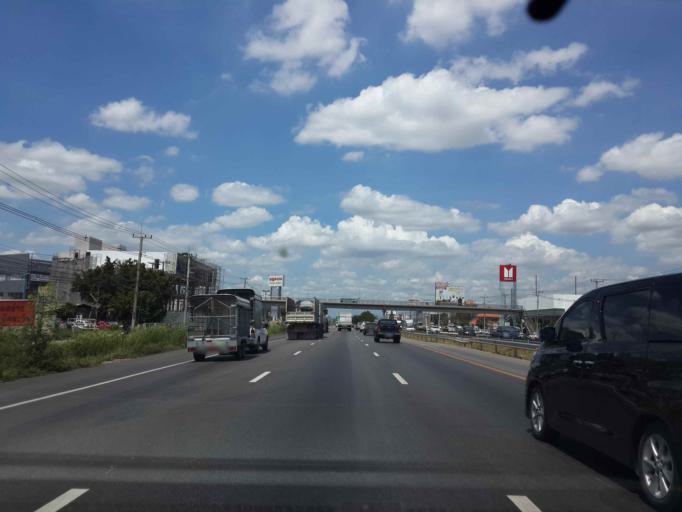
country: TH
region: Bangkok
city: Bang Bon
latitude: 13.6039
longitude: 100.3713
